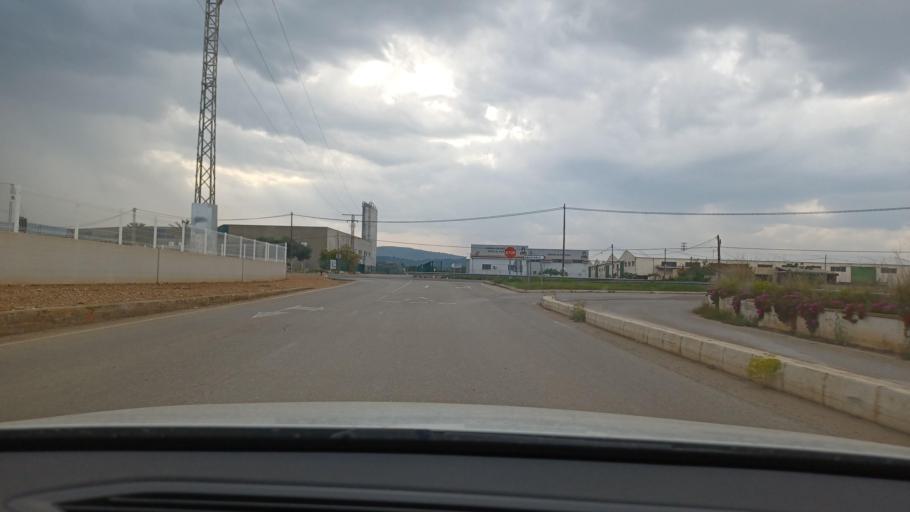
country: ES
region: Valencia
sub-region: Provincia de Castello
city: Benicarlo
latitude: 40.4095
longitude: 0.3933
